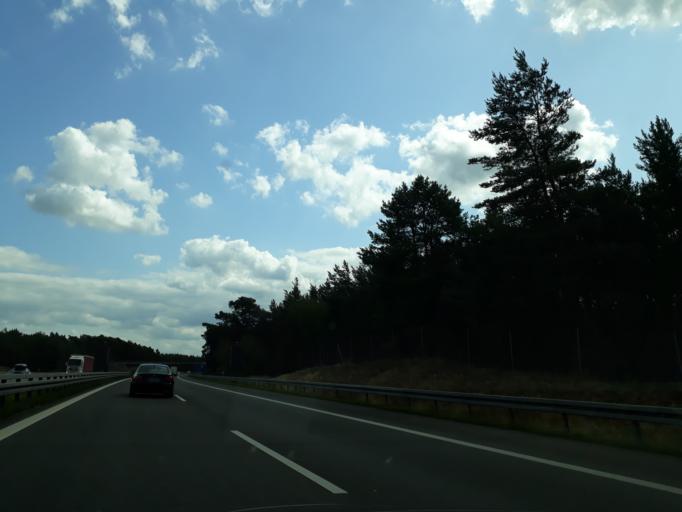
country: DE
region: Brandenburg
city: Kasel-Golzig
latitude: 52.0065
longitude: 13.7151
